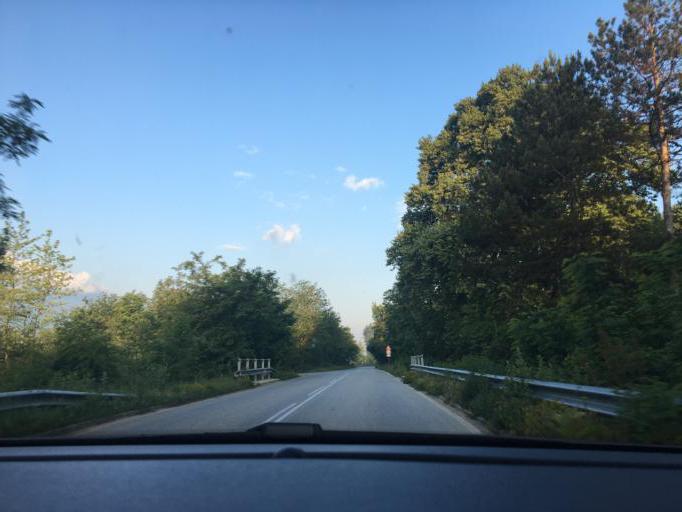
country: MK
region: Novo Selo
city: Novo Selo
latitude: 41.3963
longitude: 23.0052
